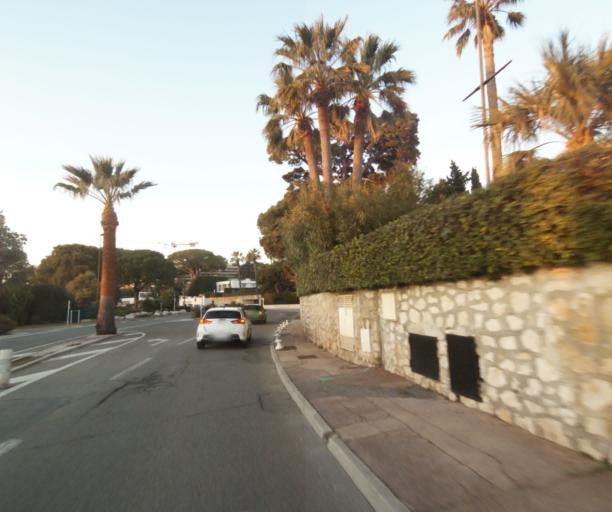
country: FR
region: Provence-Alpes-Cote d'Azur
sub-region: Departement des Alpes-Maritimes
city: Antibes
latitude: 43.5623
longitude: 7.1177
